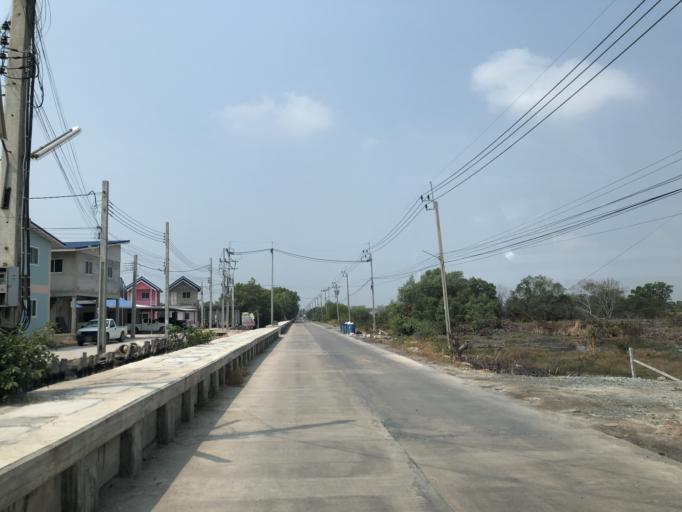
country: TH
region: Samut Prakan
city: Bang Bo
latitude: 13.5173
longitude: 100.8307
